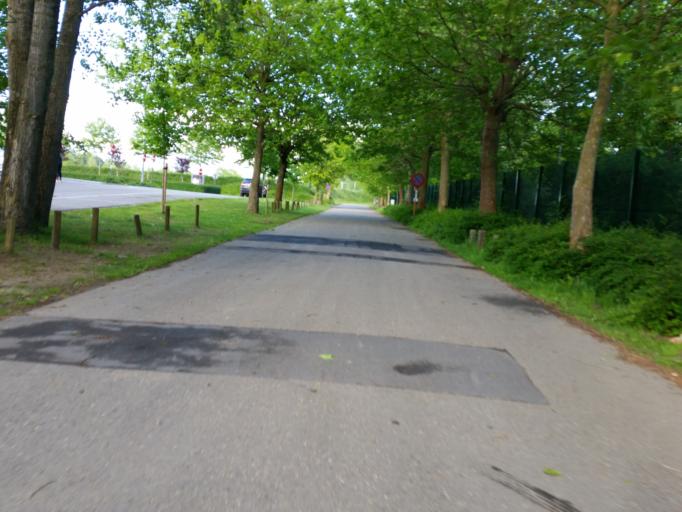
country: BE
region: Flanders
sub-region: Provincie Antwerpen
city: Mechelen
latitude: 51.0251
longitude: 4.4979
